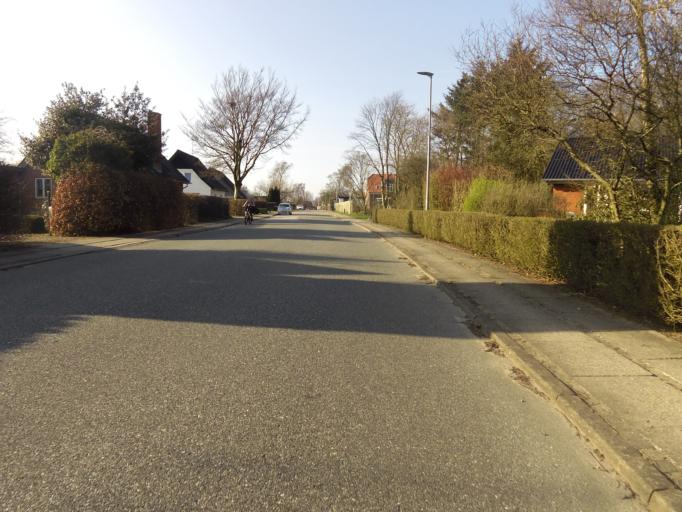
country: DK
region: South Denmark
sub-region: Vejen Kommune
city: Vejen
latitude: 55.4668
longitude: 9.1054
